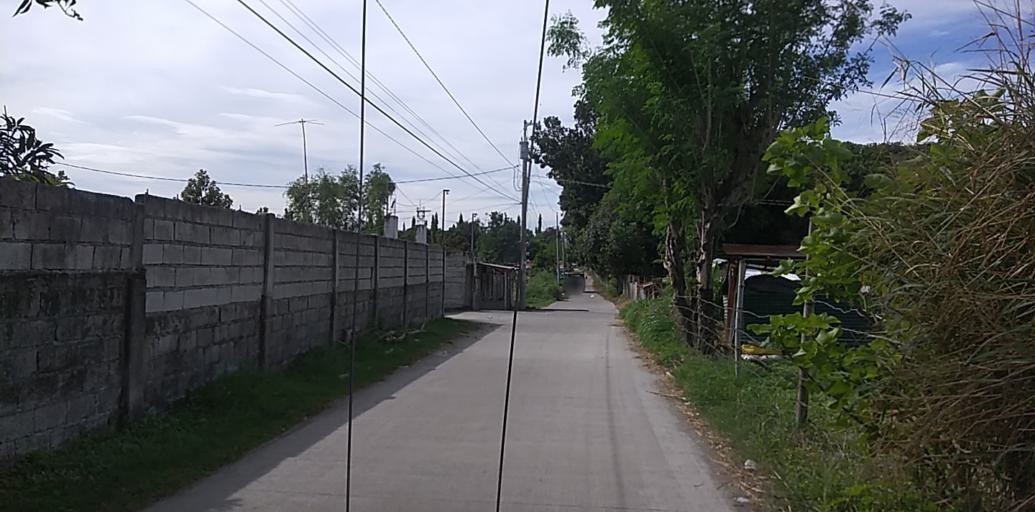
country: PH
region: Central Luzon
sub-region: Province of Pampanga
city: Angeles City
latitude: 15.1271
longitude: 120.5641
